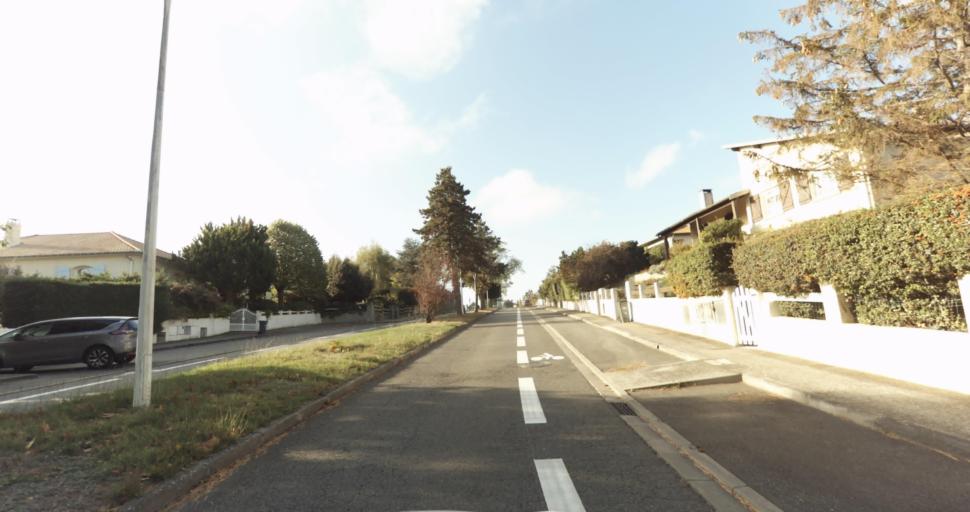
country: FR
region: Midi-Pyrenees
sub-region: Departement de la Haute-Garonne
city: Ramonville-Saint-Agne
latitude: 43.5456
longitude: 1.4645
